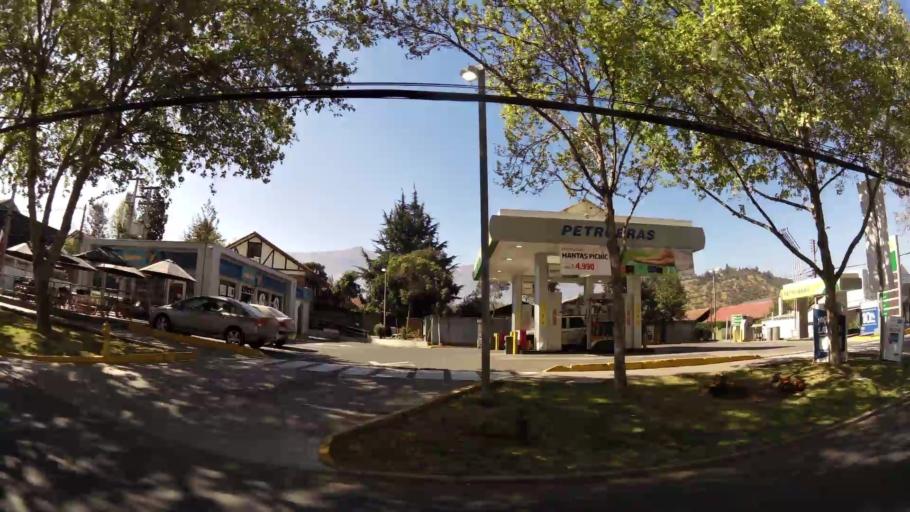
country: CL
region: Santiago Metropolitan
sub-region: Provincia de Santiago
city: Villa Presidente Frei, Nunoa, Santiago, Chile
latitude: -33.3884
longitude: -70.5395
